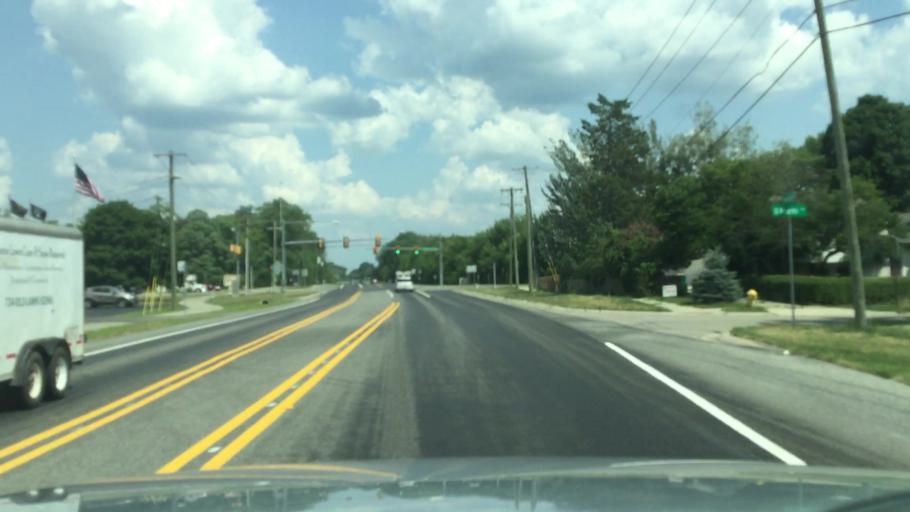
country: US
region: Michigan
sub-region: Washtenaw County
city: Ypsilanti
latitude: 42.2029
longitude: -83.5833
